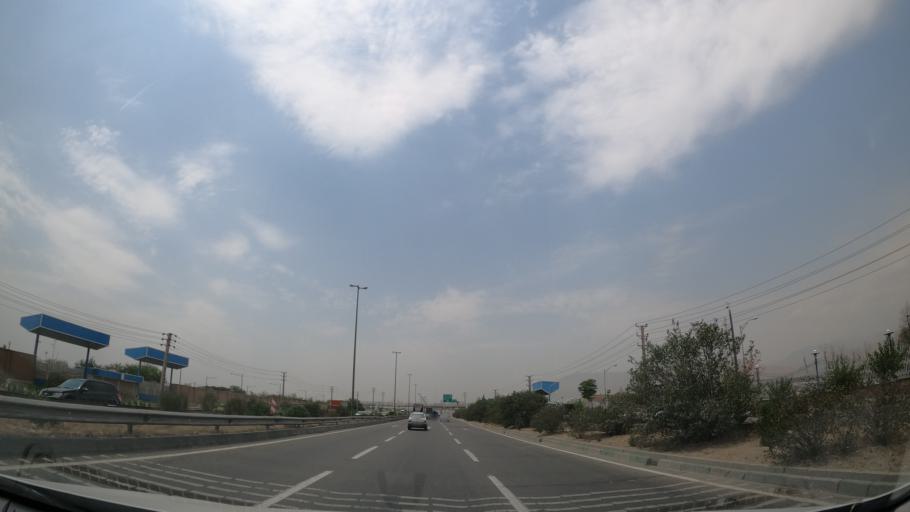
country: IR
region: Tehran
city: Shahr-e Qods
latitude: 35.7013
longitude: 51.1890
